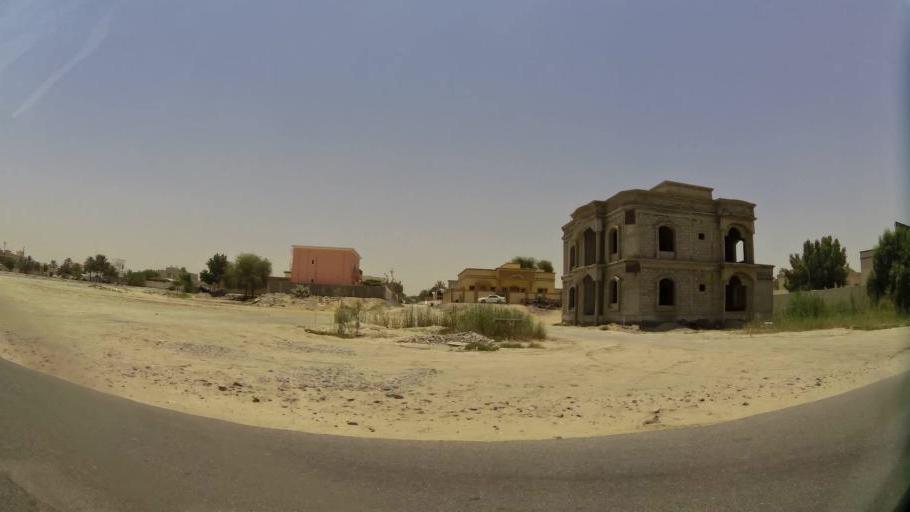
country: AE
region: Ajman
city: Ajman
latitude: 25.4051
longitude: 55.5107
